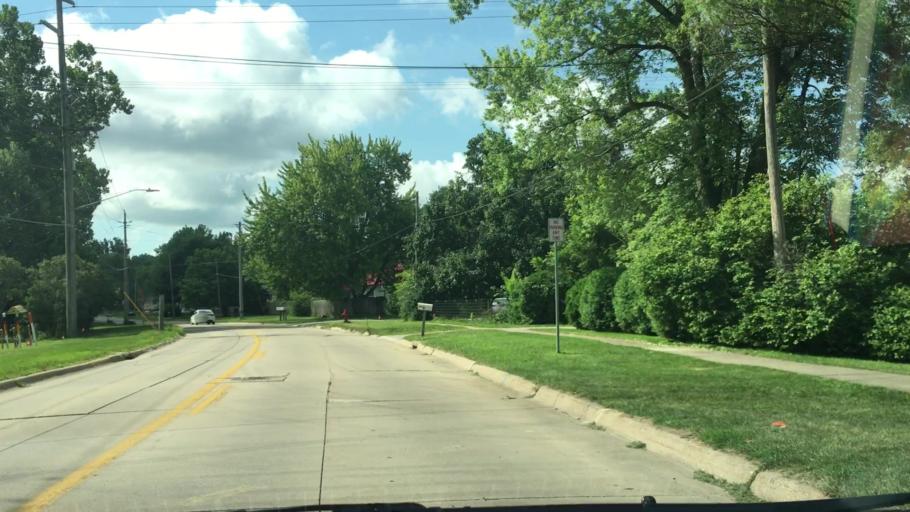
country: US
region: Iowa
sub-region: Johnson County
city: Iowa City
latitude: 41.6861
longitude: -91.5241
